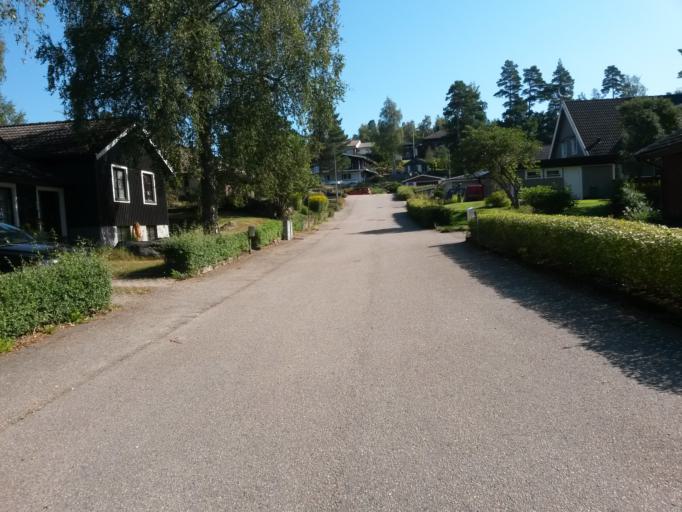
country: SE
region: Vaestra Goetaland
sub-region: Vargarda Kommun
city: Vargarda
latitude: 58.0384
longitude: 12.8205
